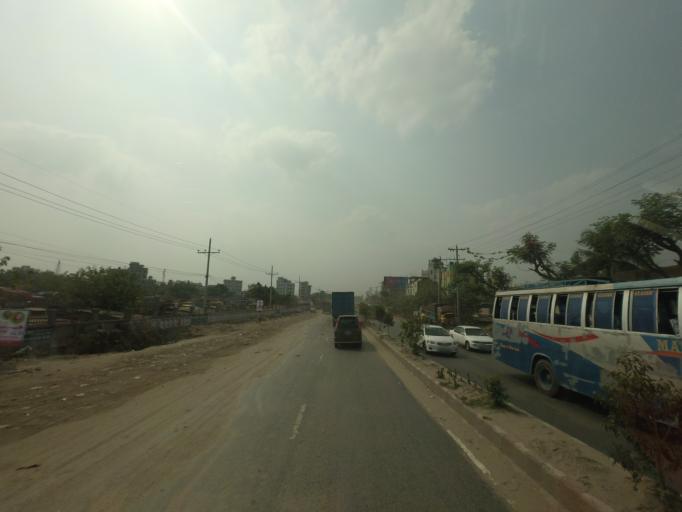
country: BD
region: Dhaka
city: Azimpur
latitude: 23.7855
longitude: 90.3318
